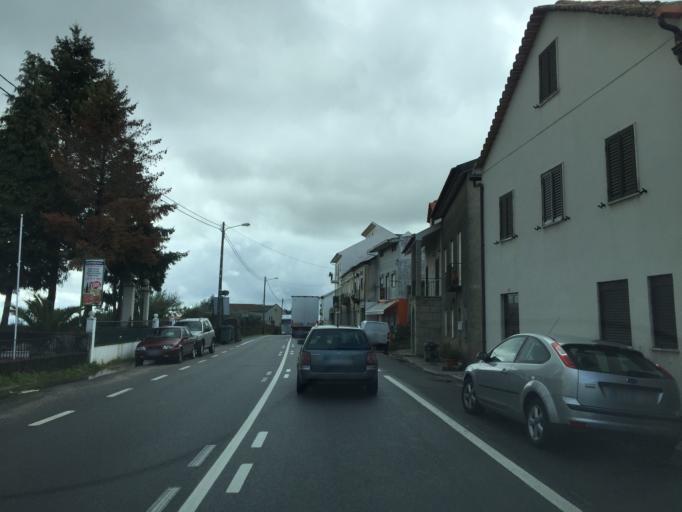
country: PT
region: Coimbra
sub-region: Oliveira do Hospital
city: Oliveira do Hospital
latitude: 40.3152
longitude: -7.8967
